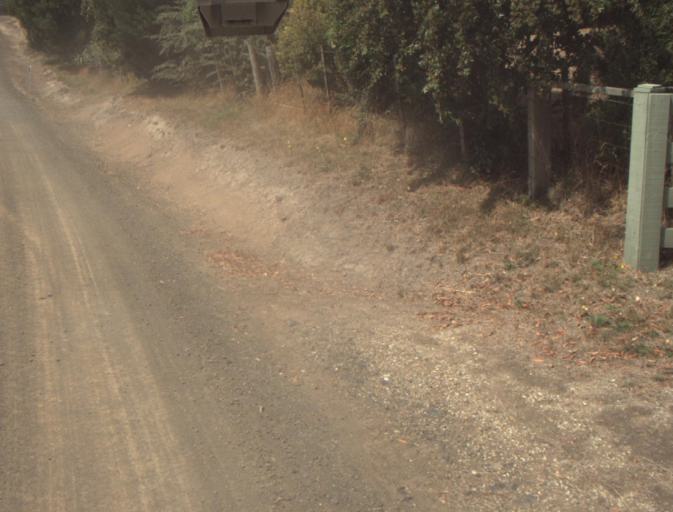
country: AU
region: Tasmania
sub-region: Launceston
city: Mayfield
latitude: -41.2362
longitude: 147.1249
